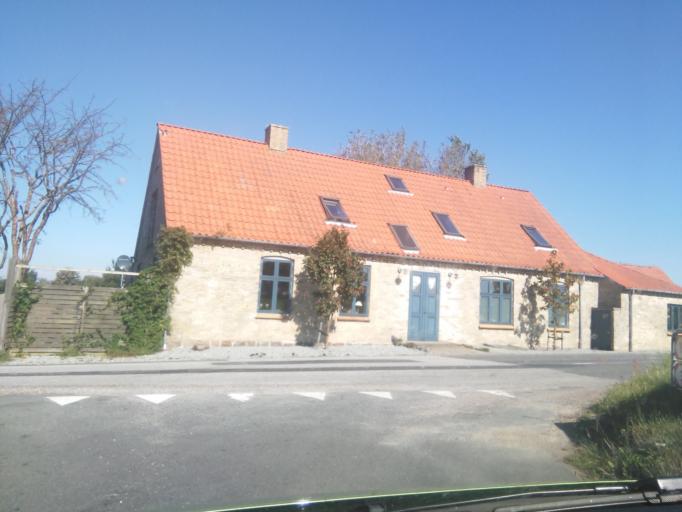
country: DK
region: Central Jutland
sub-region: Syddjurs Kommune
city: Ronde
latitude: 56.1965
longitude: 10.4691
